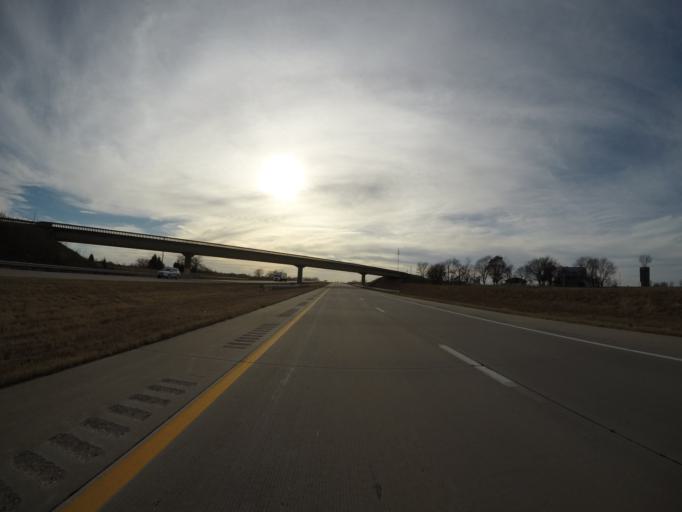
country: US
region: Kansas
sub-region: Franklin County
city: Wellsville
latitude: 38.6955
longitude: -95.1037
